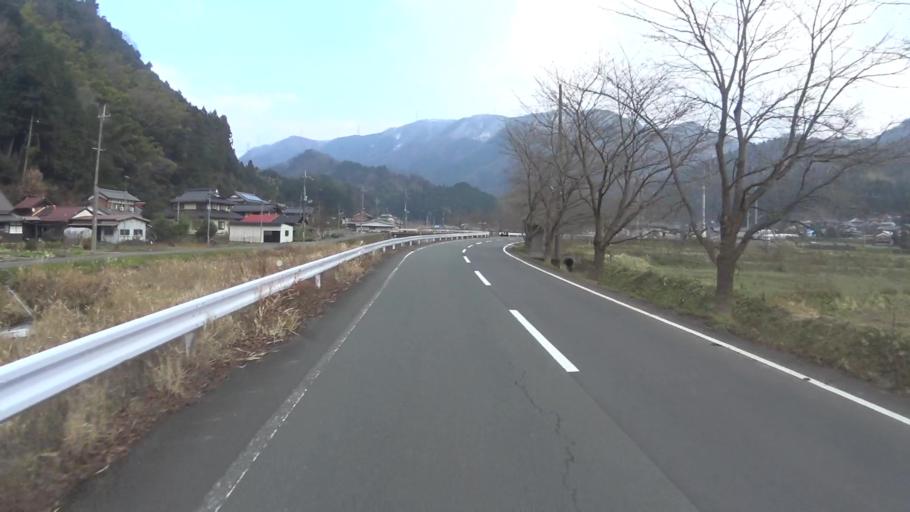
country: JP
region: Kyoto
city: Maizuru
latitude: 35.4476
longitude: 135.4246
